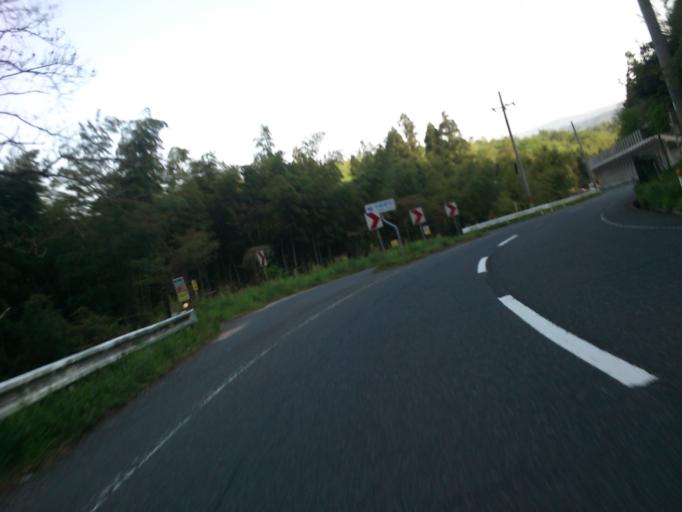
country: JP
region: Kyoto
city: Miyazu
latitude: 35.5913
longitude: 135.1606
